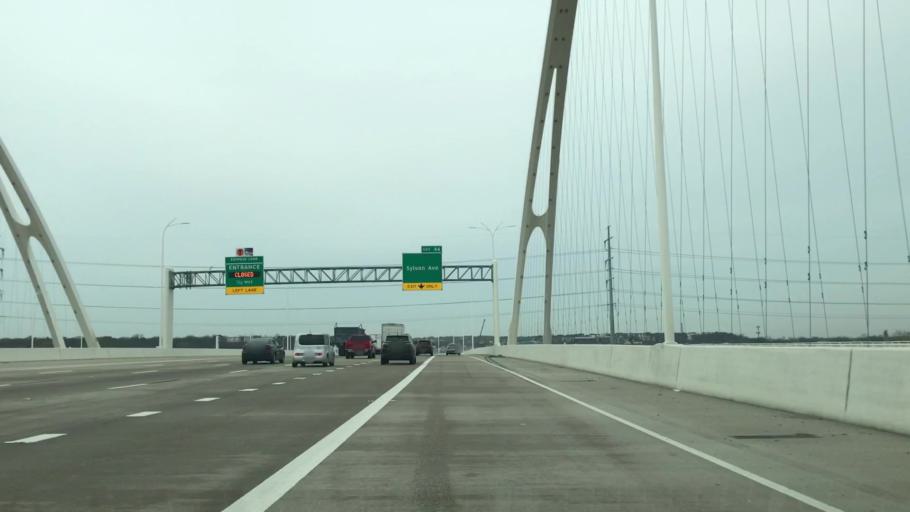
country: US
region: Texas
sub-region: Dallas County
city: Dallas
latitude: 32.7707
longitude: -96.8174
